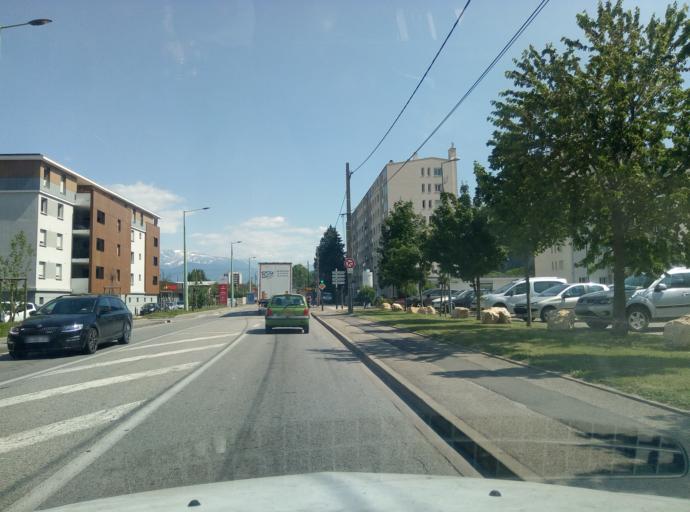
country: FR
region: Rhone-Alpes
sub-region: Departement de l'Isere
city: Sassenage
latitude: 45.2003
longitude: 5.6691
